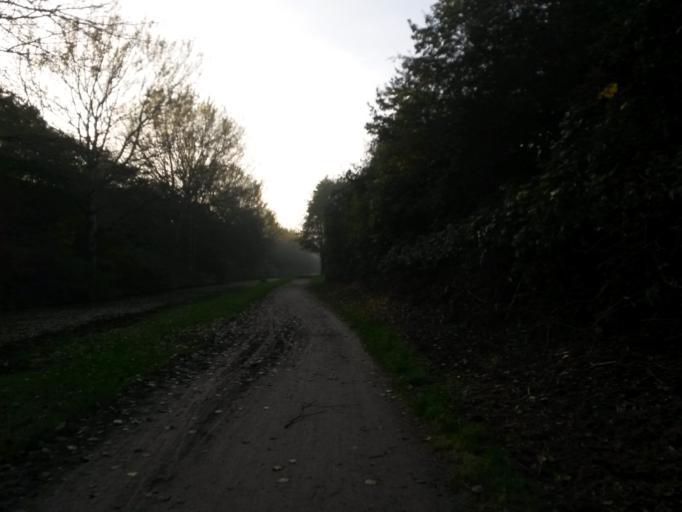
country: DE
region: Bremen
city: Bremen
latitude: 53.0245
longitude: 8.8360
